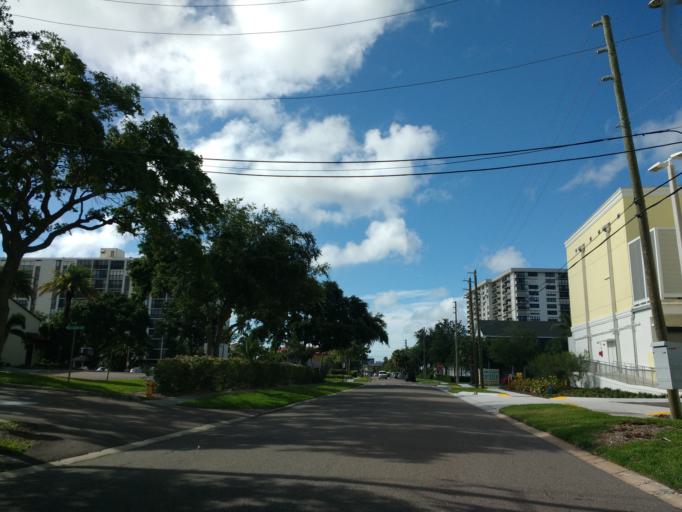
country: US
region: Florida
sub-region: Pinellas County
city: Clearwater
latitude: 27.9787
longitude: -82.8176
